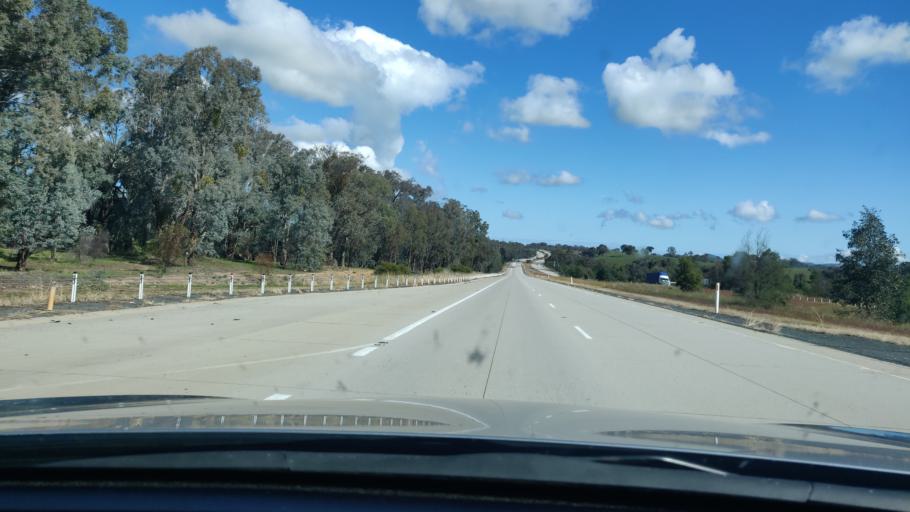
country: AU
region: New South Wales
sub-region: Greater Hume Shire
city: Holbrook
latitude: -35.8330
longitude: 147.2193
